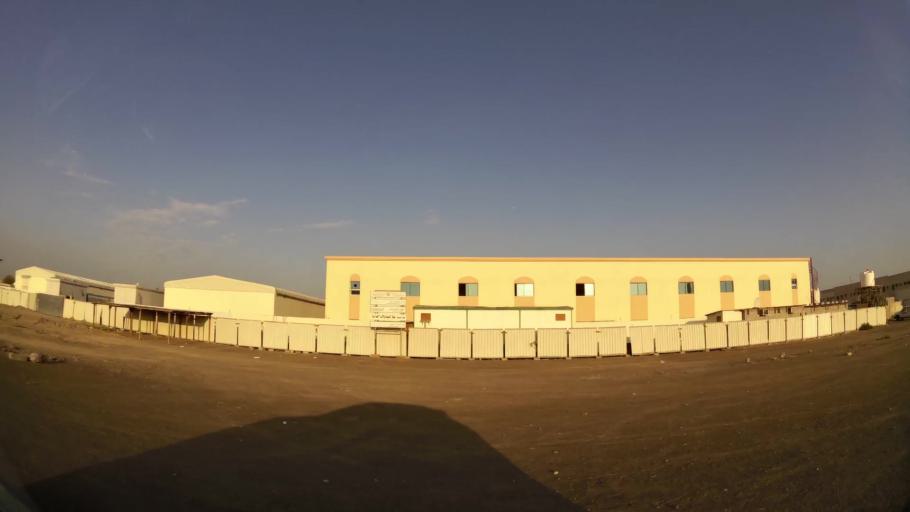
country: AE
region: Abu Dhabi
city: Al Ain
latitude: 24.1541
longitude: 55.8222
